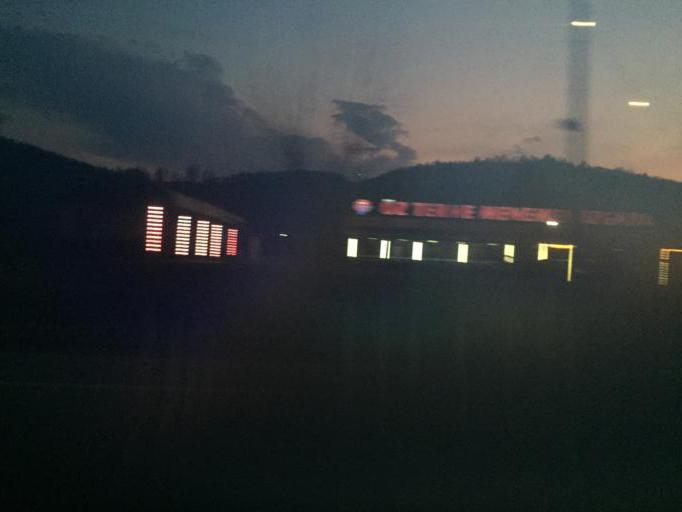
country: TR
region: Samsun
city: Kavak
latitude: 41.1364
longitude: 36.1258
